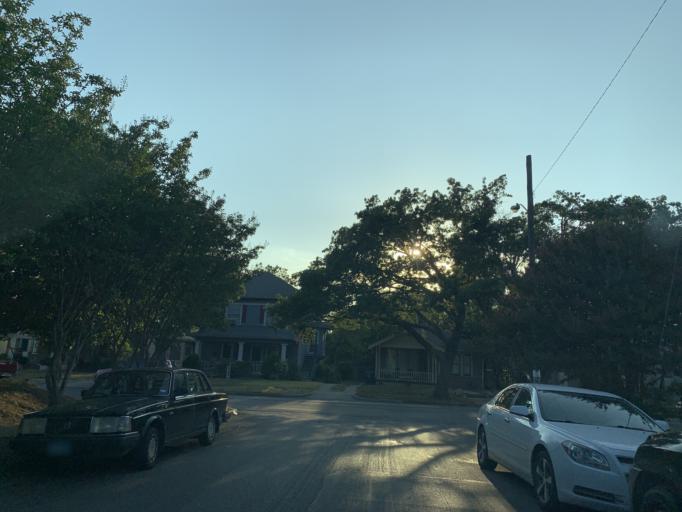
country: US
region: Texas
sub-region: Dallas County
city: Cockrell Hill
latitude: 32.7478
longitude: -96.8512
